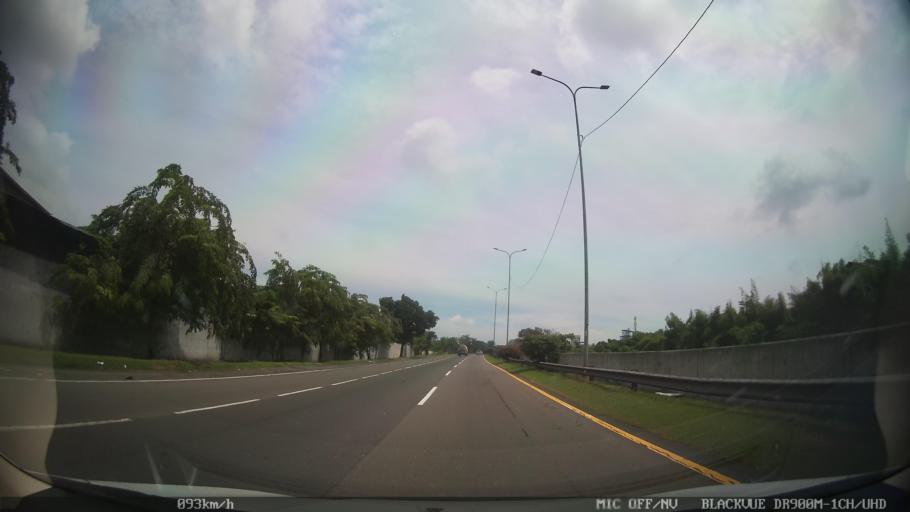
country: ID
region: North Sumatra
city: Labuhan Deli
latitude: 3.6748
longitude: 98.6802
